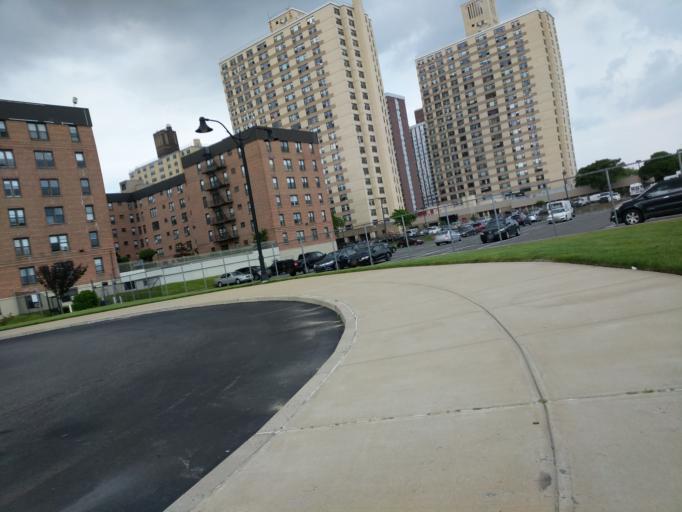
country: US
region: New York
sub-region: Nassau County
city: Atlantic Beach
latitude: 40.5926
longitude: -73.7556
